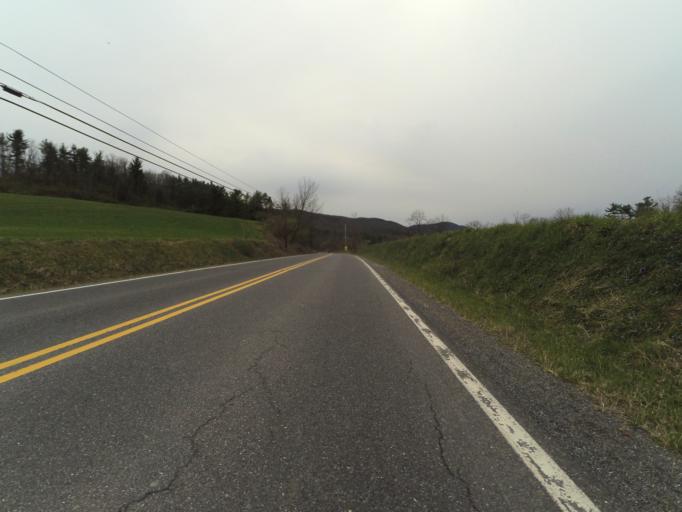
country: US
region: Pennsylvania
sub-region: Centre County
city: Milesburg
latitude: 40.9592
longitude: -77.7473
